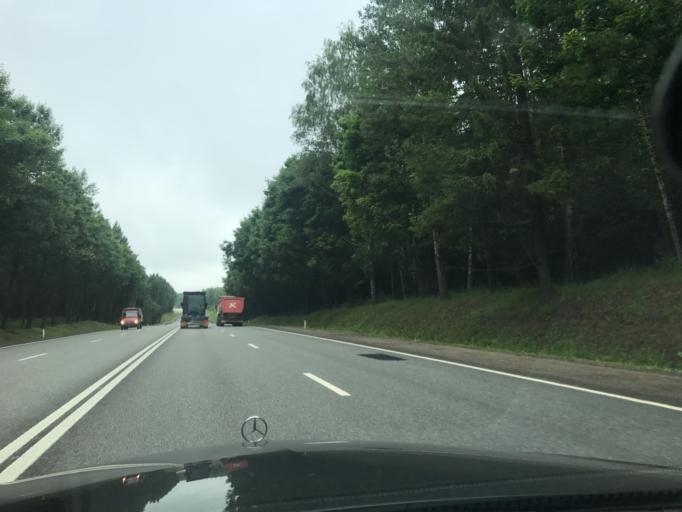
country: RU
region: Smolensk
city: Vyaz'ma
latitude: 55.3184
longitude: 34.5416
